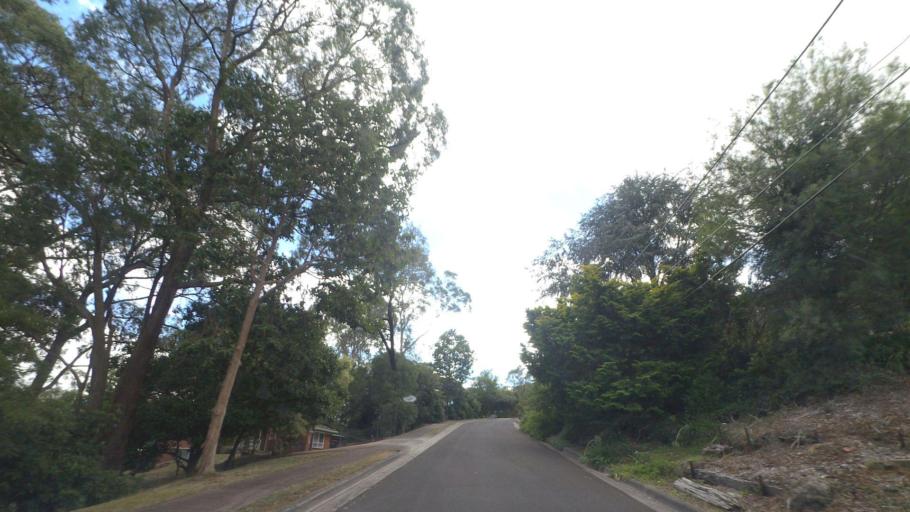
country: AU
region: Victoria
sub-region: Knox
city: Ferntree Gully
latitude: -37.8709
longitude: 145.3056
